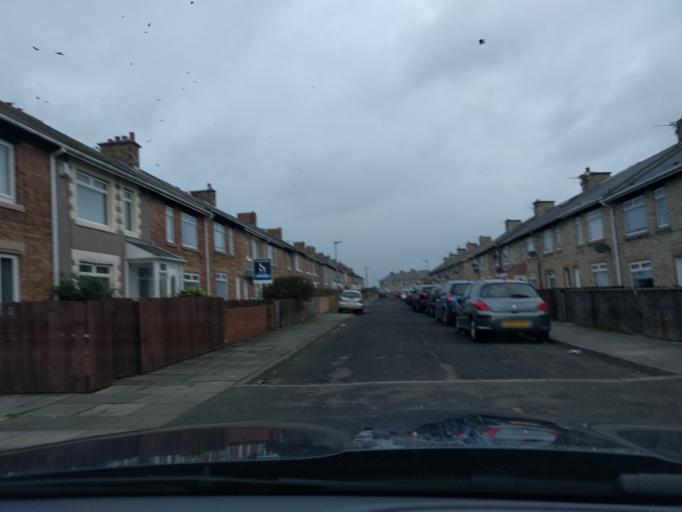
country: GB
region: England
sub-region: Northumberland
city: Newbiggin-by-the-Sea
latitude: 55.1861
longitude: -1.5209
